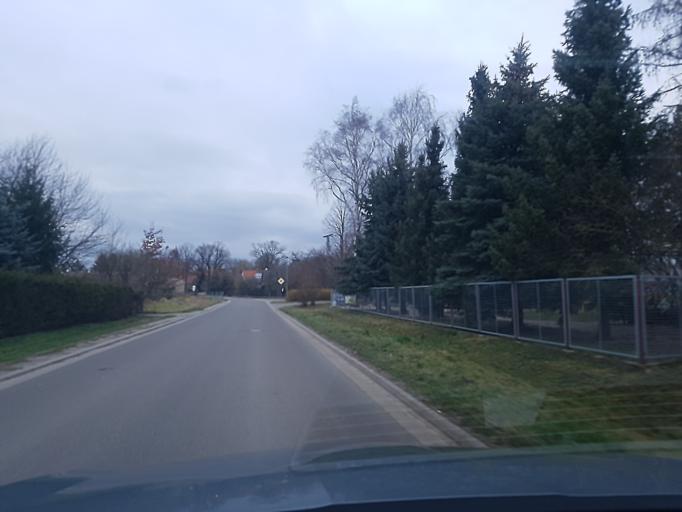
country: DE
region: Brandenburg
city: Sonnewalde
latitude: 51.6879
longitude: 13.6826
